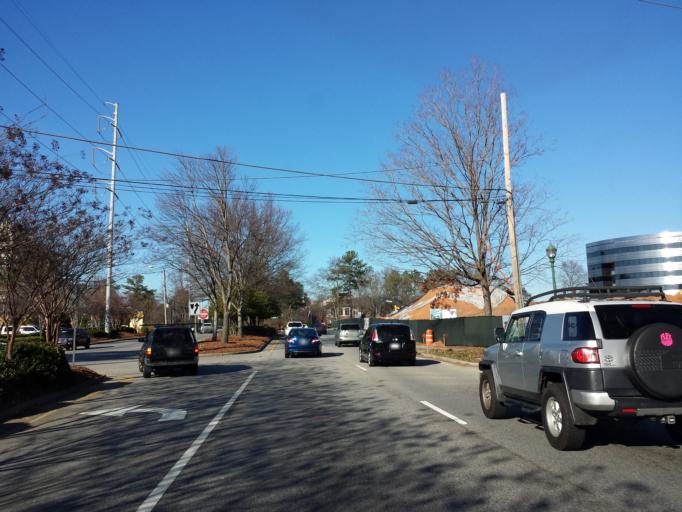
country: US
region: Georgia
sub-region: DeKalb County
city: Dunwoody
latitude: 33.9270
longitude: -84.3370
